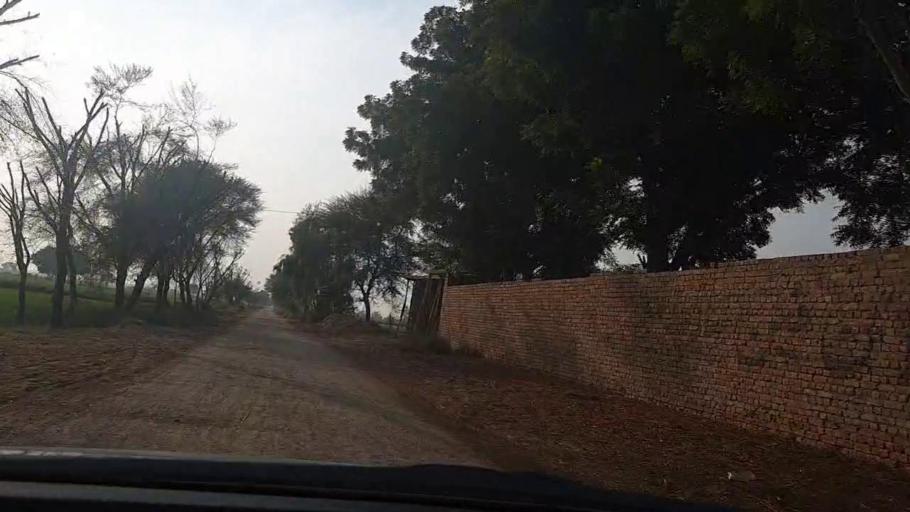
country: PK
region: Sindh
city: Daulatpur
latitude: 26.3369
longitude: 68.0265
